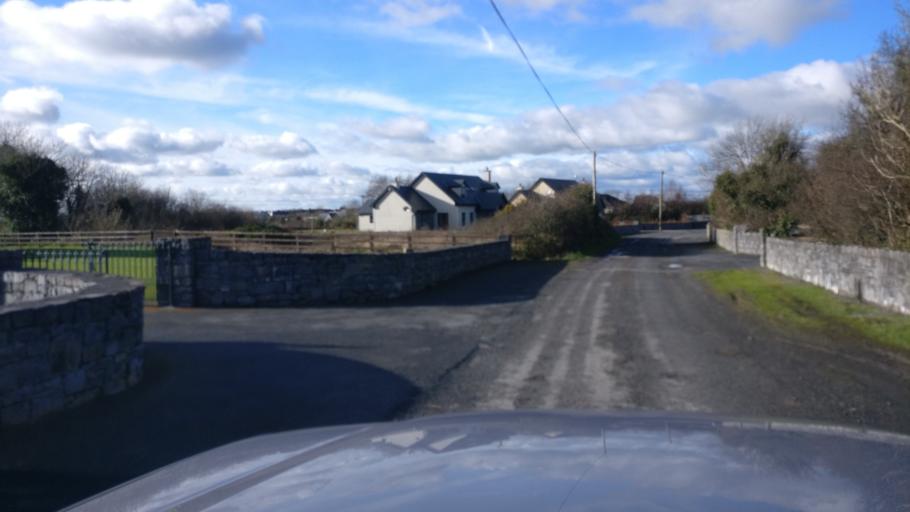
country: IE
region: Connaught
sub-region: County Galway
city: Athenry
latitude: 53.2252
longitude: -8.8091
